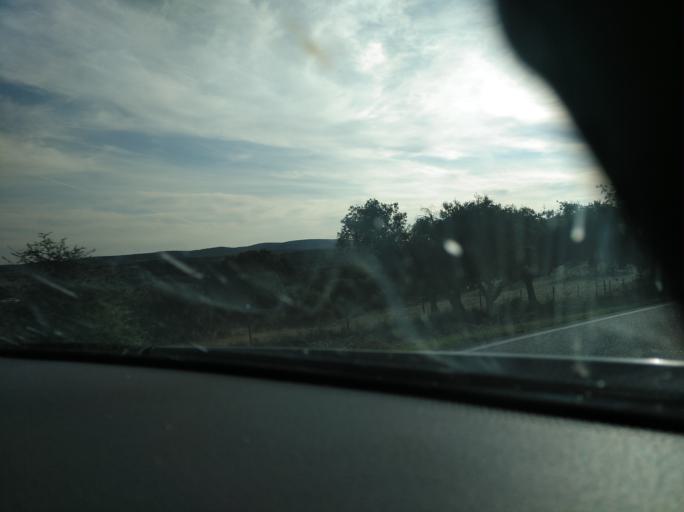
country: PT
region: Portalegre
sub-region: Fronteira
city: Fronteira
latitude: 38.9620
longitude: -7.6028
